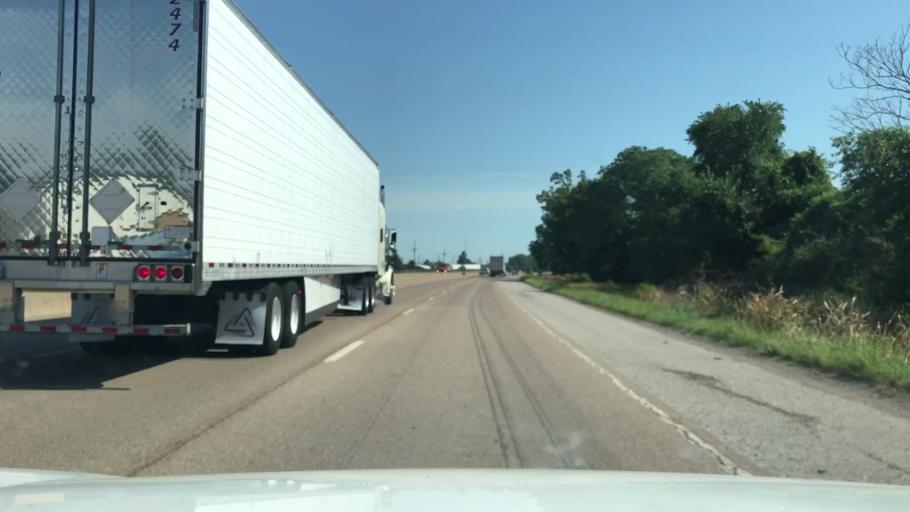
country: US
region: Illinois
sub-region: Madison County
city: Venice
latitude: 38.6853
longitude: -90.1722
